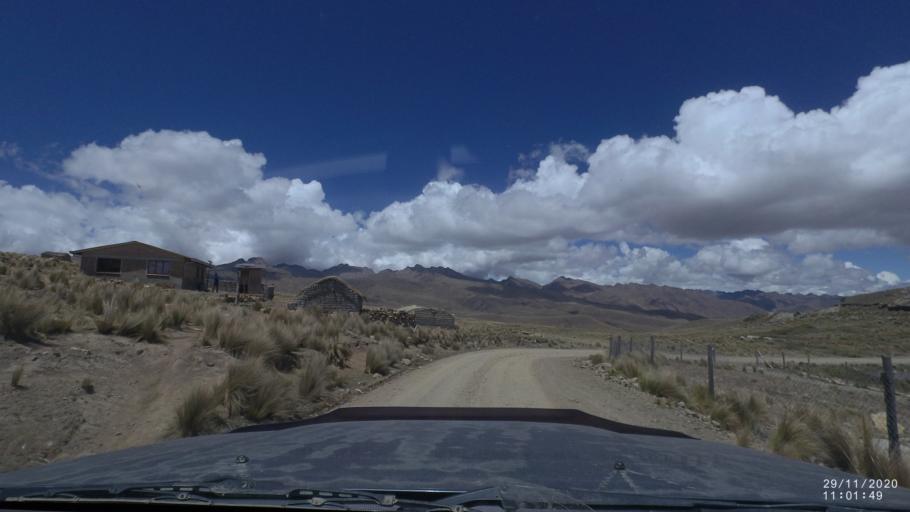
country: BO
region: Cochabamba
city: Cochabamba
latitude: -17.1968
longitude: -66.2239
